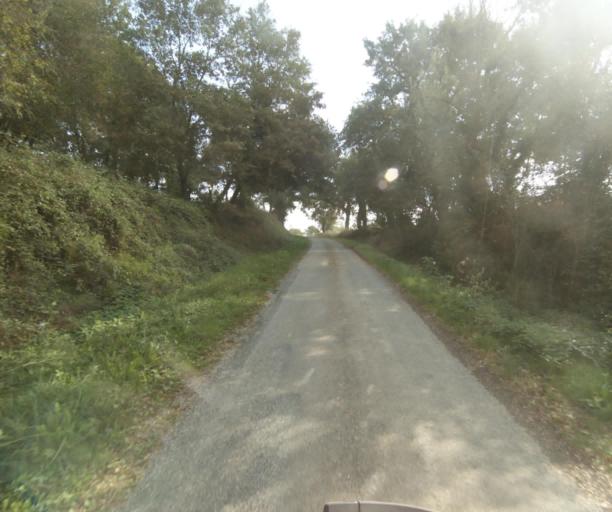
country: FR
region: Midi-Pyrenees
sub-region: Departement du Tarn-et-Garonne
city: Verdun-sur-Garonne
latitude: 43.8481
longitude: 1.1674
